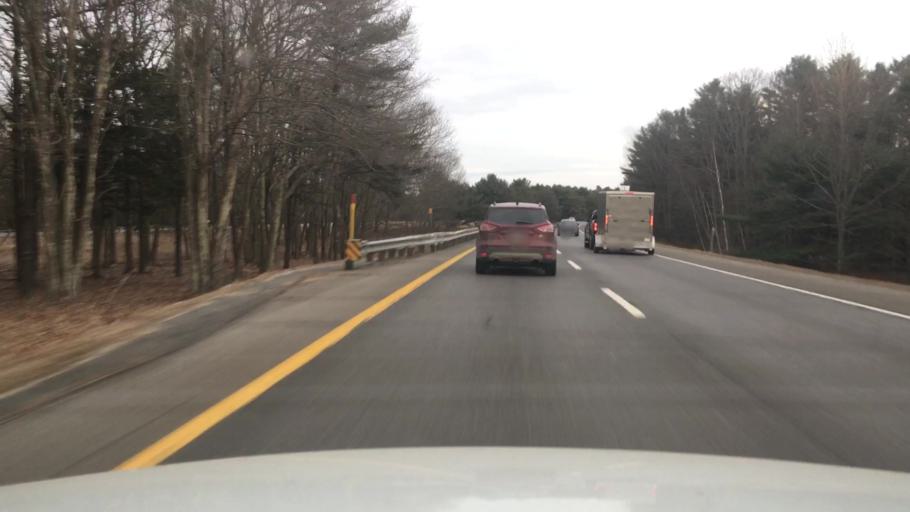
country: US
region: Maine
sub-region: Sagadahoc County
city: Bath
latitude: 43.9181
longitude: -69.8895
